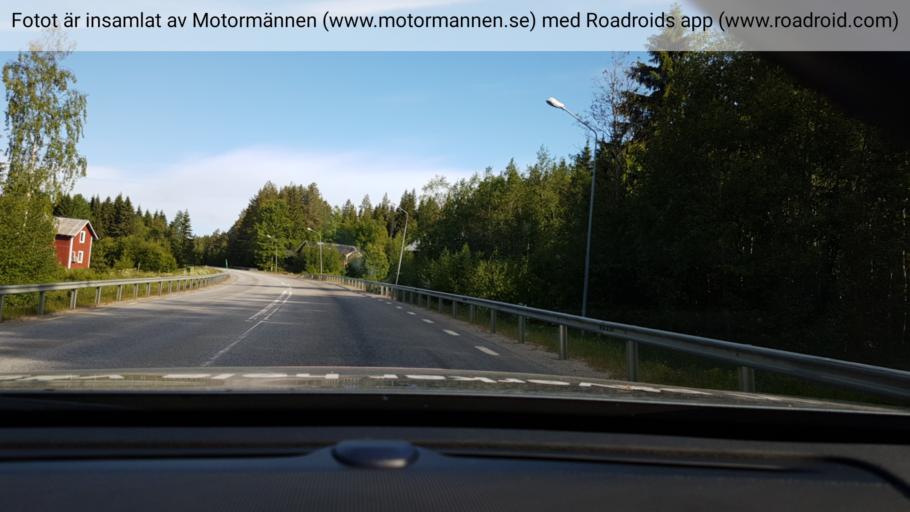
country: SE
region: Vaesterbotten
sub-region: Vannas Kommun
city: Vaennaes
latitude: 63.9637
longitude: 19.7511
